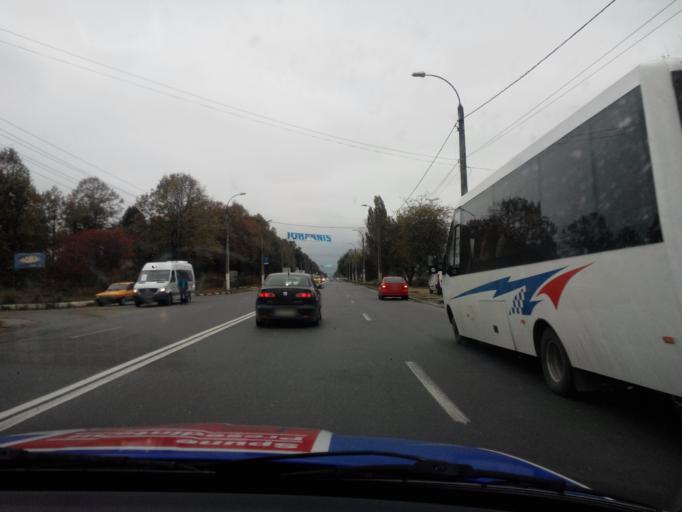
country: RO
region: Giurgiu
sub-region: Comuna Fratesti
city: Remus
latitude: 43.9215
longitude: 25.9735
